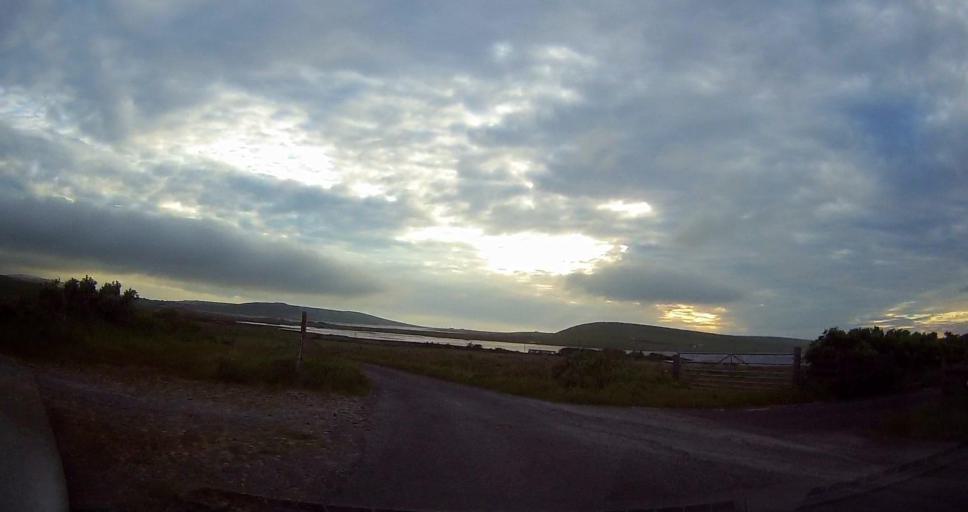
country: GB
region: Scotland
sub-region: Orkney Islands
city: Stromness
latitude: 59.1095
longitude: -3.2222
